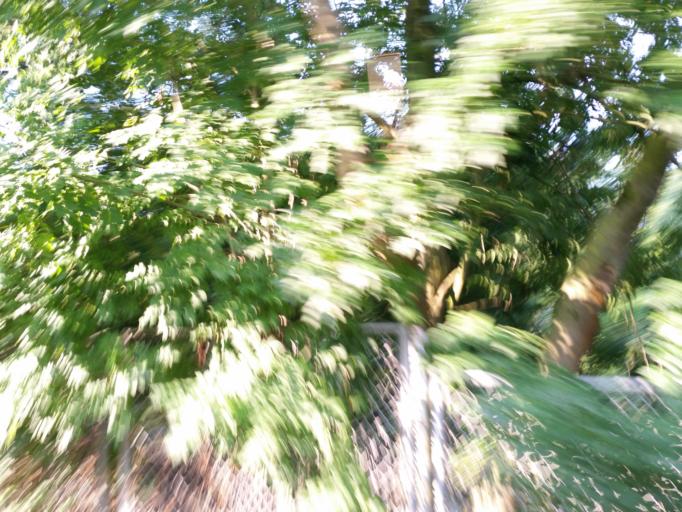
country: NL
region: South Holland
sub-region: Gemeente Leerdam
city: Leerdam
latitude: 51.8805
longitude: 5.1115
